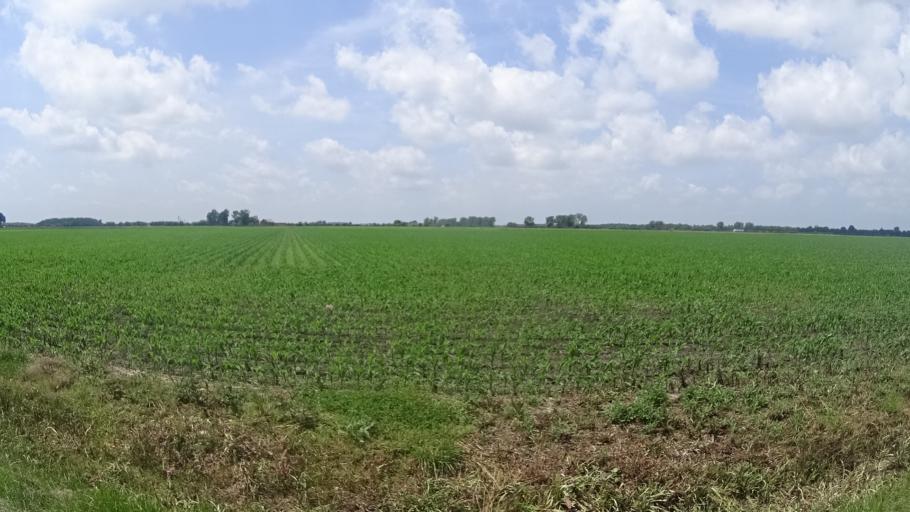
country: US
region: Ohio
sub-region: Huron County
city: Bellevue
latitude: 41.3081
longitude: -82.7637
